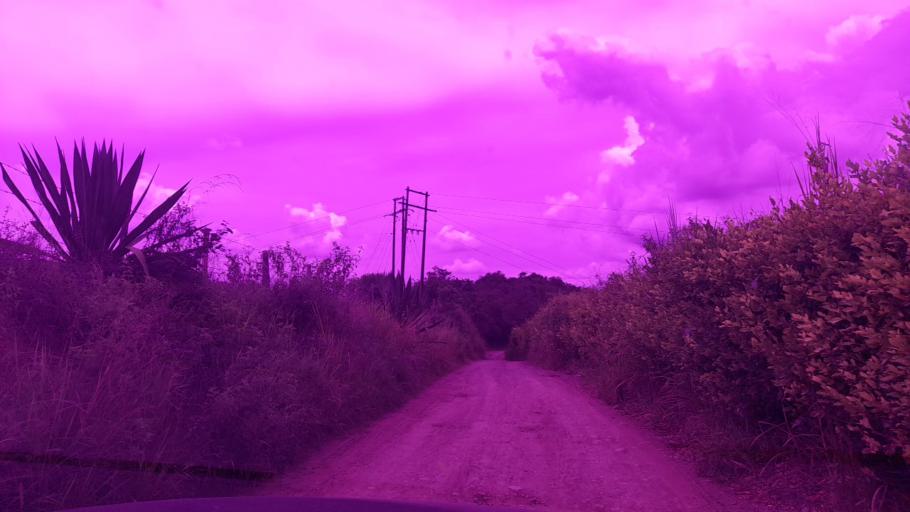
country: CO
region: Valle del Cauca
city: Andalucia
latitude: 4.1726
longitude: -76.1194
